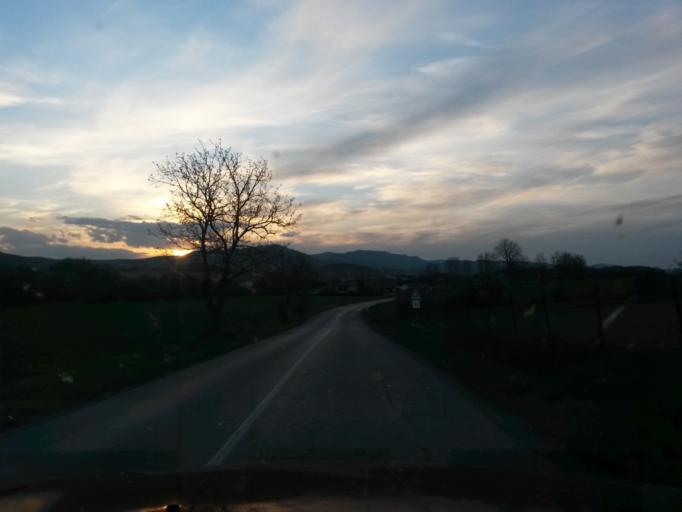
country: HU
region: Borsod-Abauj-Zemplen
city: Satoraljaujhely
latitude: 48.5173
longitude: 21.5969
